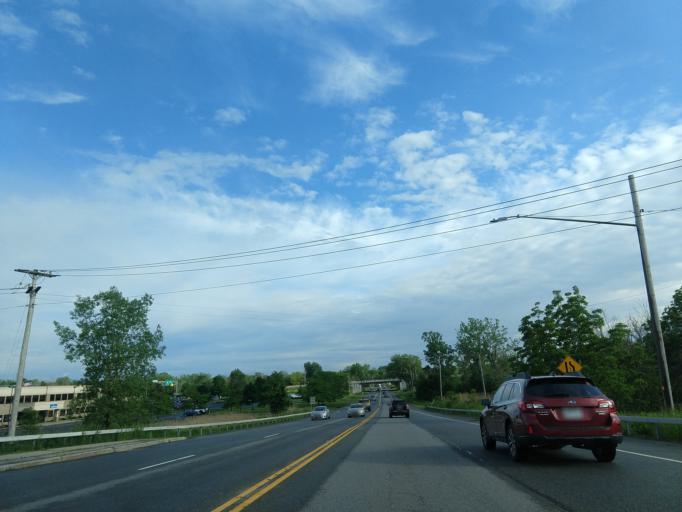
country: US
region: New York
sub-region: Erie County
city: West Seneca
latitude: 42.8528
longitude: -78.7879
